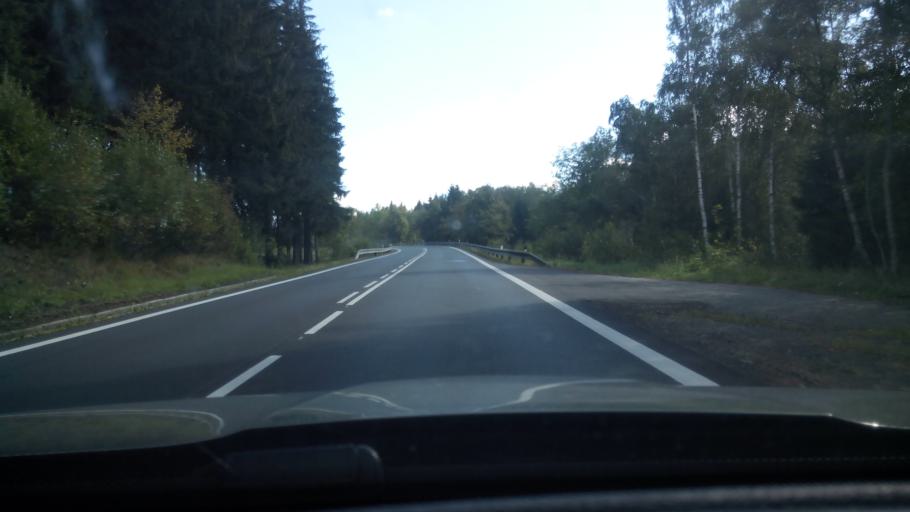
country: CZ
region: Jihocesky
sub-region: Okres Prachatice
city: Zdikov
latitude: 49.0696
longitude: 13.7164
